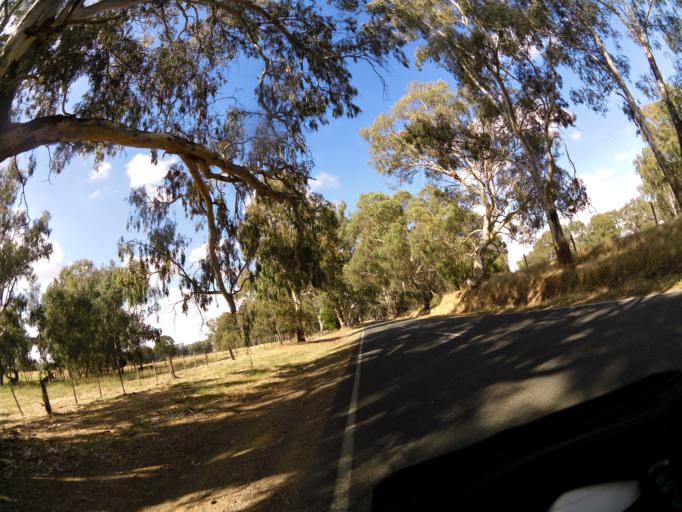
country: AU
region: Victoria
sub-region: Benalla
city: Benalla
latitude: -36.5677
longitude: 145.9931
